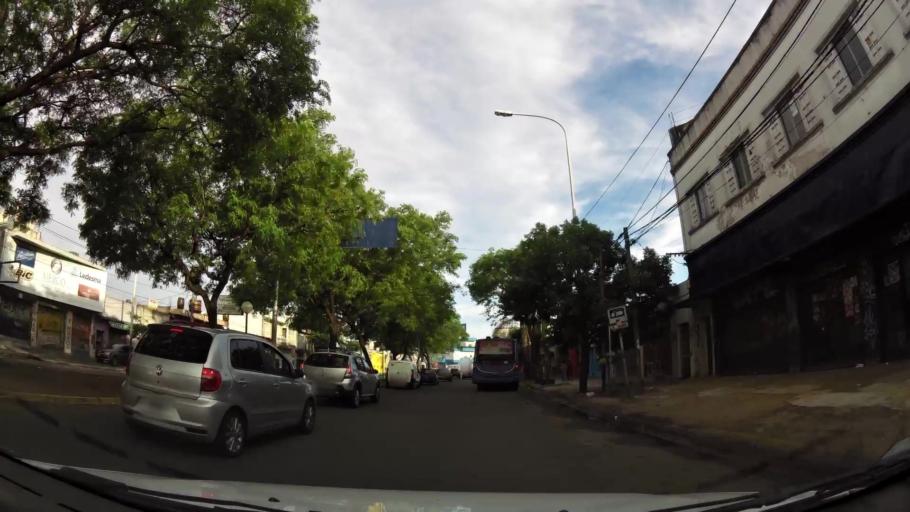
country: AR
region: Buenos Aires
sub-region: Partido de Moron
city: Moron
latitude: -34.6416
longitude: -58.6237
